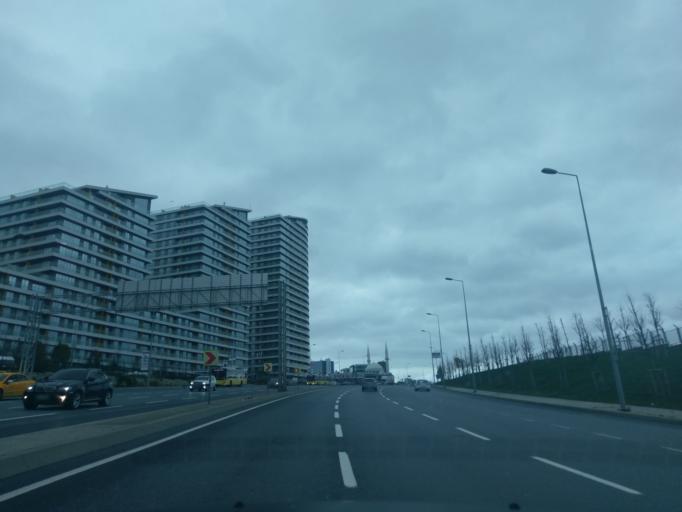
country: TR
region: Istanbul
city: Mahmutbey
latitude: 41.0651
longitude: 28.8420
